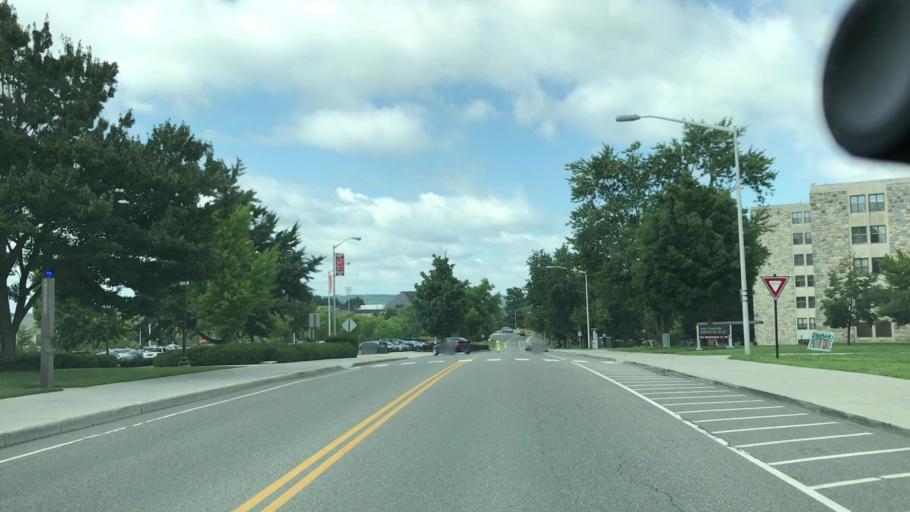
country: US
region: Virginia
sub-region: Montgomery County
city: Blacksburg
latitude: 37.2230
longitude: -80.4197
